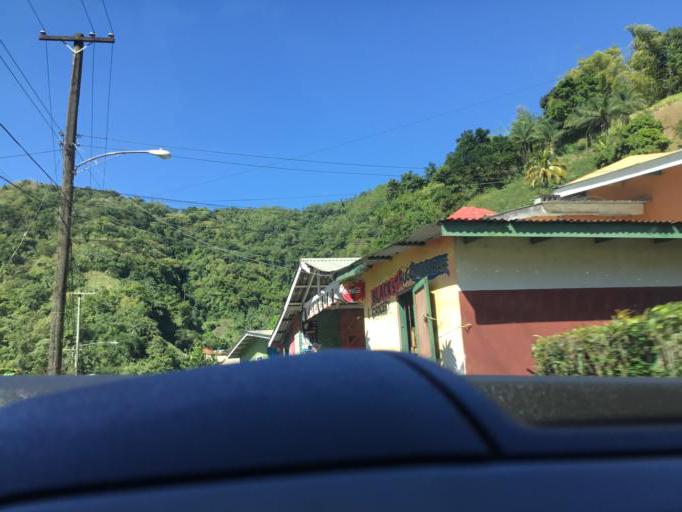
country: VC
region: Saint David
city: Chateaubelair
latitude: 13.2609
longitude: -61.2502
